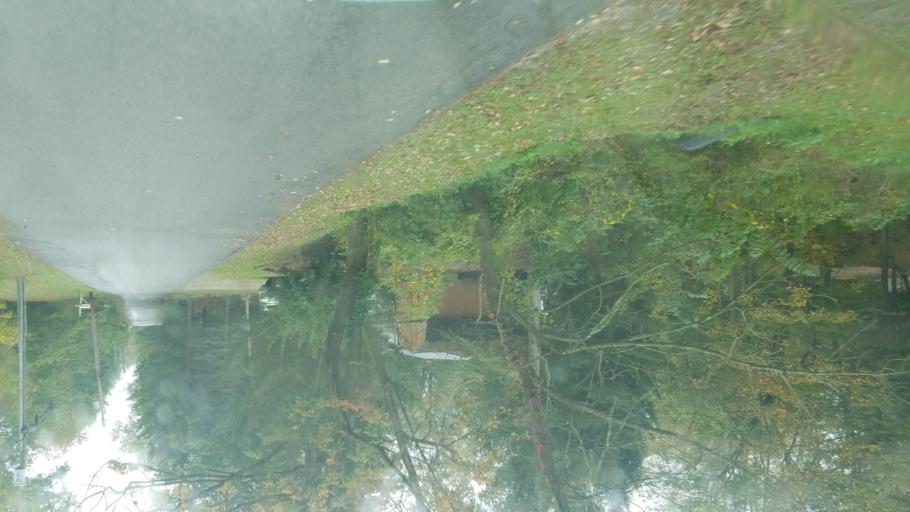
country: US
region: Ohio
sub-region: Holmes County
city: Millersburg
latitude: 40.5656
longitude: -81.8749
